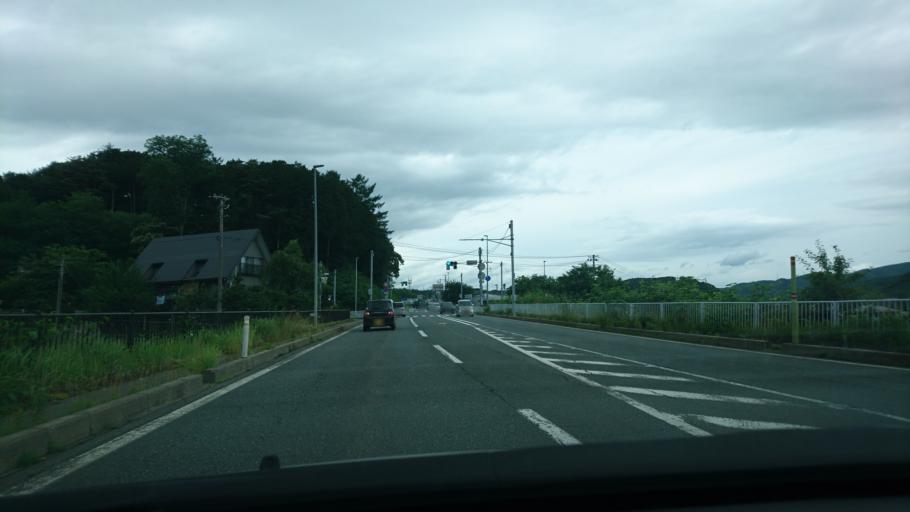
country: JP
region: Iwate
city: Morioka-shi
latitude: 39.9578
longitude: 141.2110
